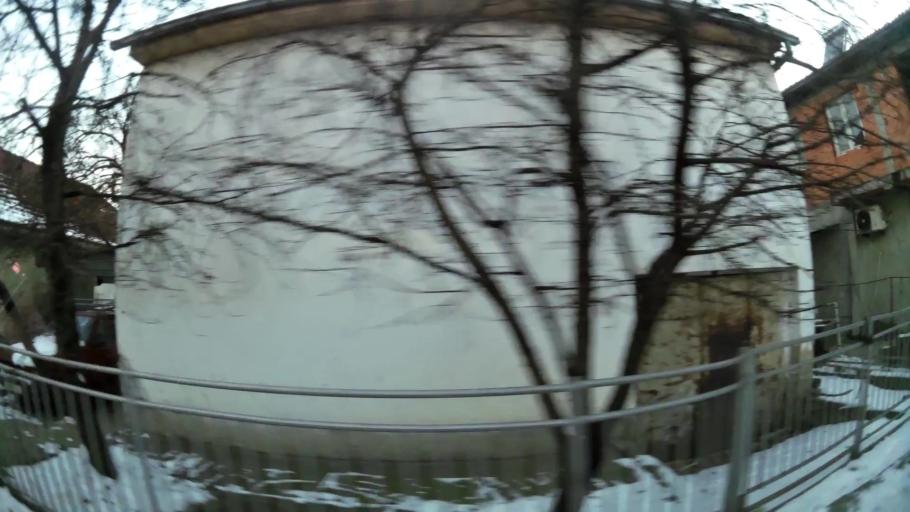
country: MK
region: Kisela Voda
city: Usje
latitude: 41.9823
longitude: 21.4846
